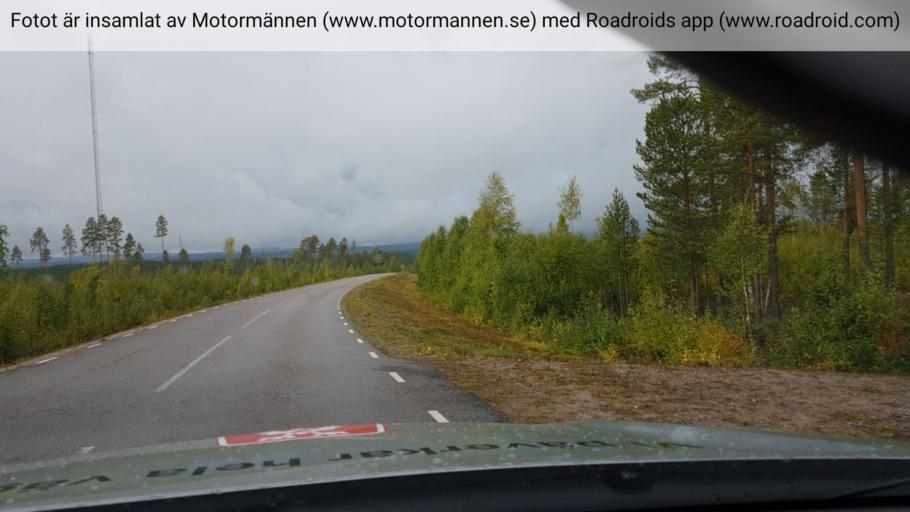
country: SE
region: Norrbotten
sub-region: Alvsbyns Kommun
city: AElvsbyn
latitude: 66.2379
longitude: 20.9314
